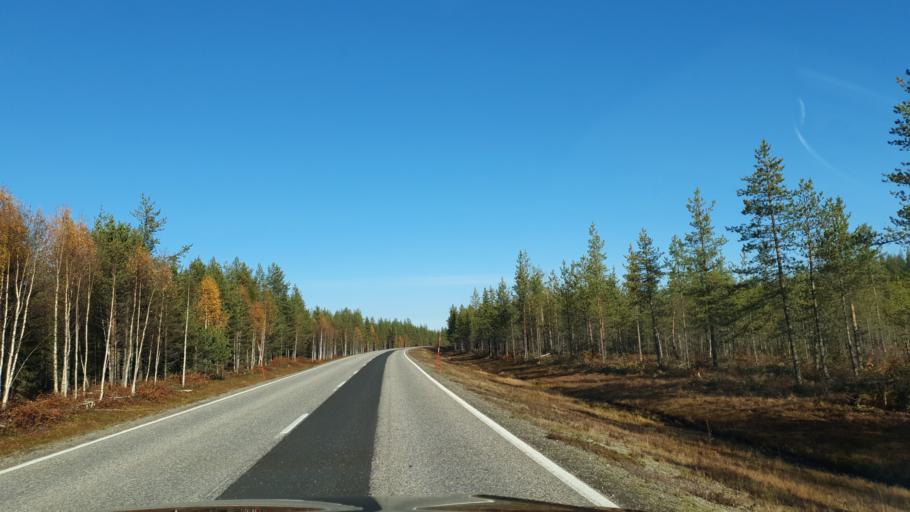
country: FI
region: Lapland
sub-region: Tunturi-Lappi
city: Kittilae
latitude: 67.3669
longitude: 24.8895
